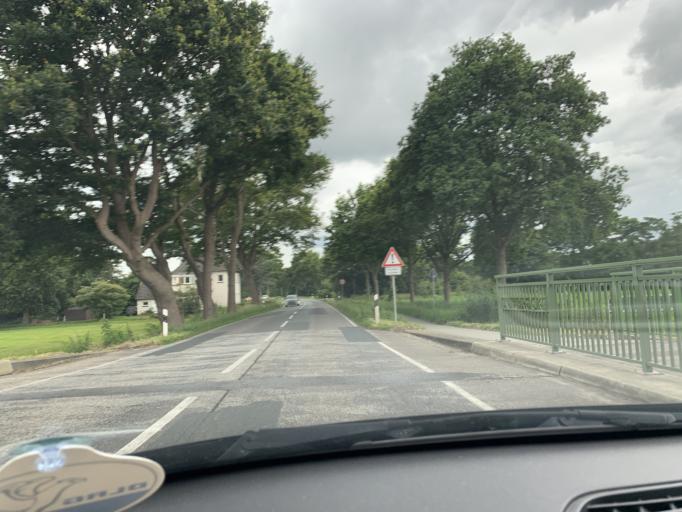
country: DE
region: Lower Saxony
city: Edewecht
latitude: 53.1180
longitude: 7.9605
